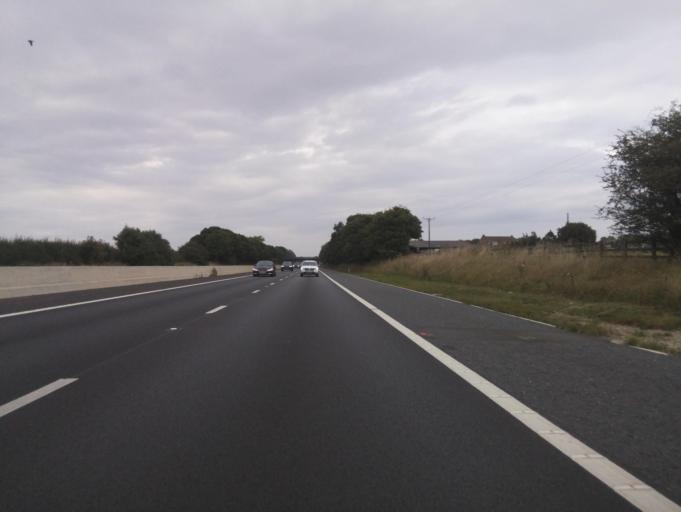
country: GB
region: England
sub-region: Darlington
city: Coatham Mundeville
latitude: 54.6012
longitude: -1.5387
